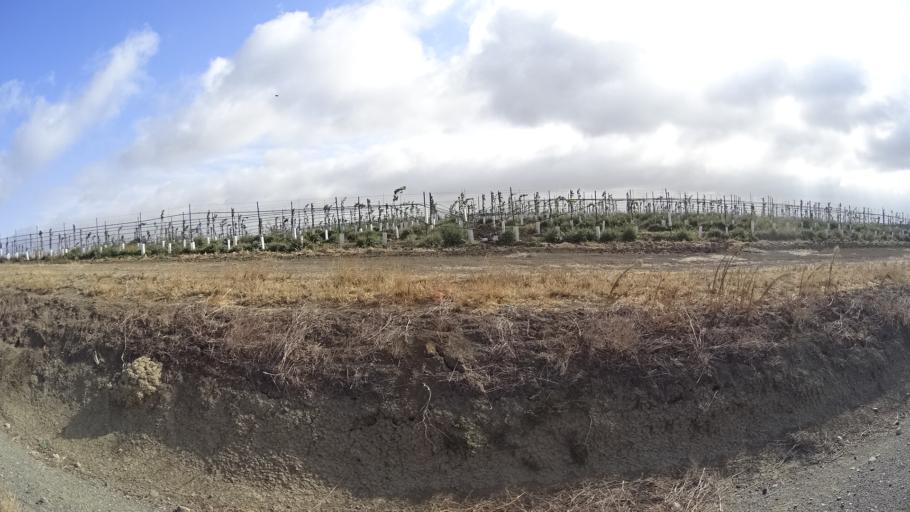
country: US
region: California
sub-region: Yolo County
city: Dunnigan
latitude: 38.7953
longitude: -122.0074
